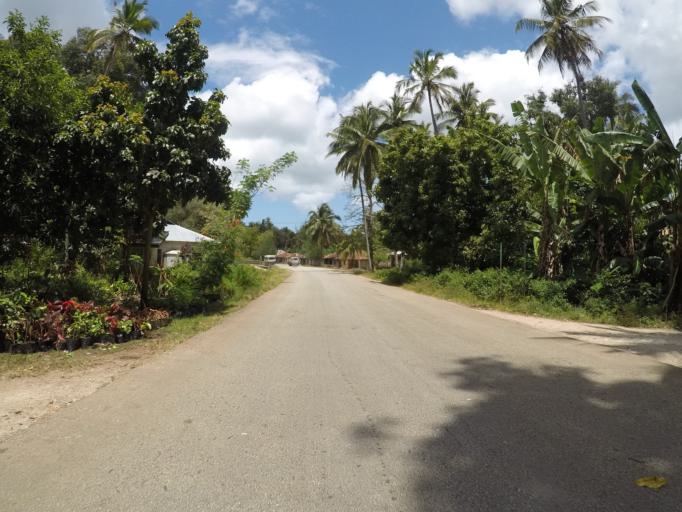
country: TZ
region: Zanzibar Central/South
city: Mahonda
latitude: -6.3017
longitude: 39.4326
